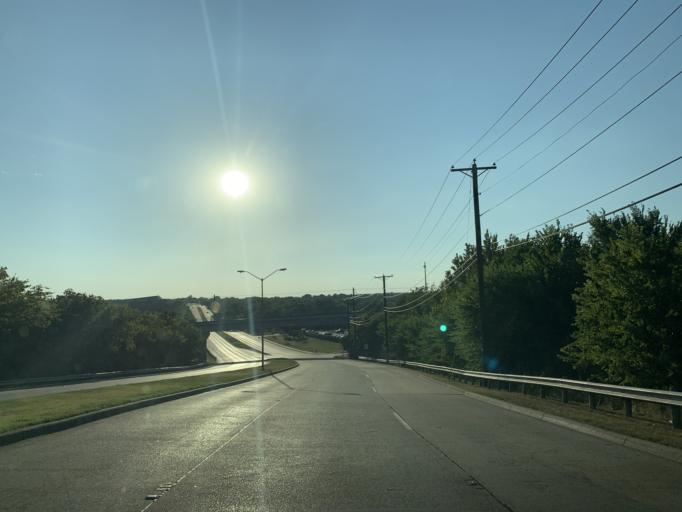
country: US
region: Texas
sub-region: Dallas County
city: Hutchins
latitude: 32.6627
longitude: -96.7860
